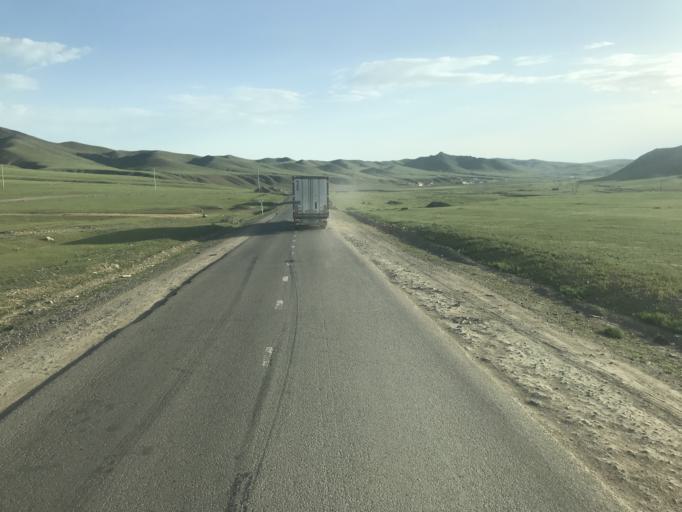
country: MN
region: Central Aimak
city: Bornuur
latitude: 48.4295
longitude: 106.1929
